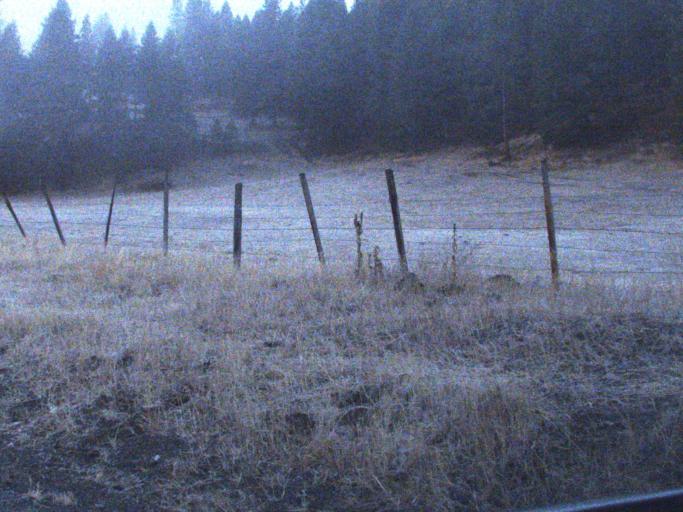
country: US
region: Washington
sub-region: Ferry County
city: Republic
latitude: 48.5848
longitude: -118.7424
